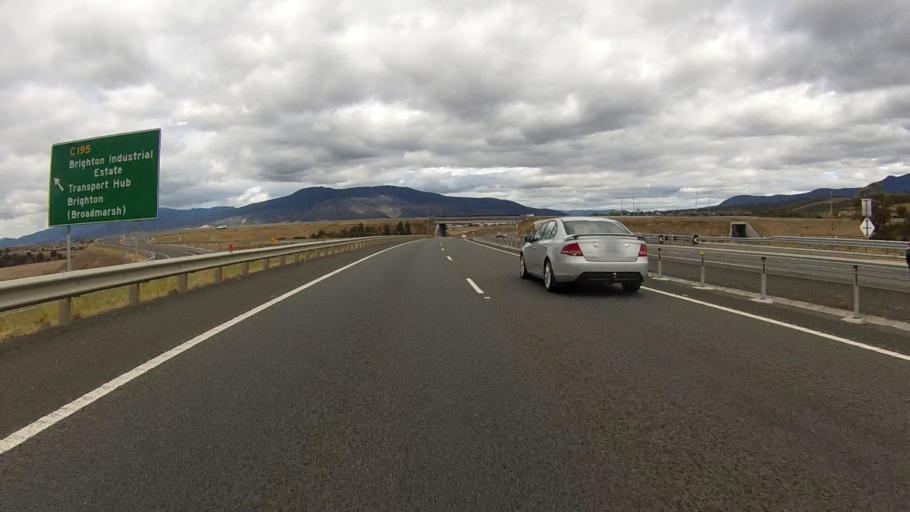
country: AU
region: Tasmania
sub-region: Brighton
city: Bridgewater
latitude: -42.7122
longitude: 147.2470
